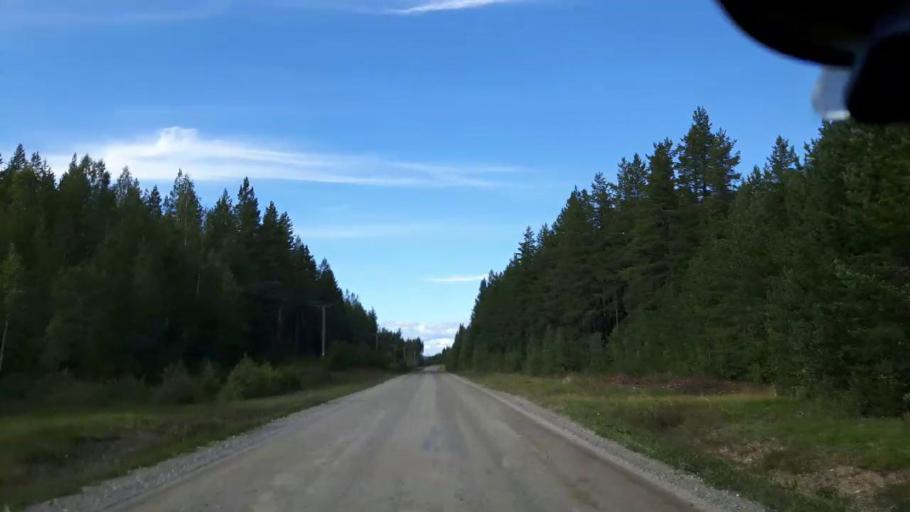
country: SE
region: Jaemtland
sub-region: Ragunda Kommun
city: Hammarstrand
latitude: 63.1386
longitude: 16.2368
